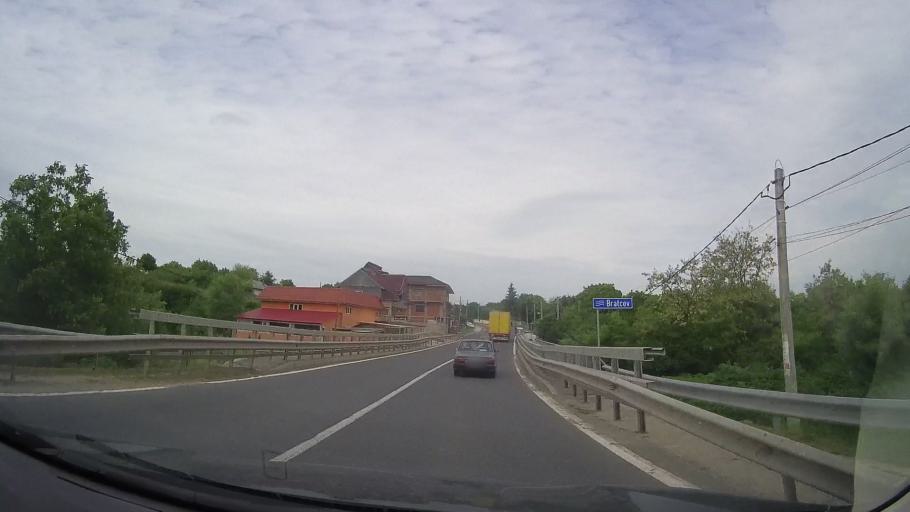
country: RO
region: Teleorman
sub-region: Comuna Maldaeni
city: Maldaeni
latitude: 44.1198
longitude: 24.9292
